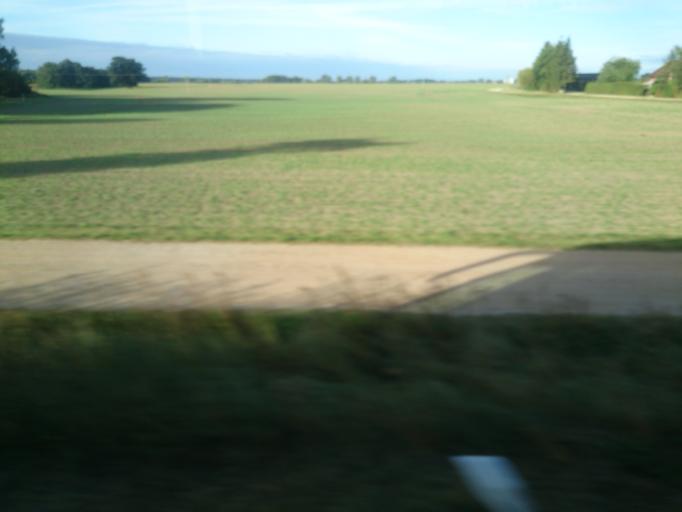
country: DE
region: Mecklenburg-Vorpommern
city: Zussow
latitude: 53.9832
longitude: 13.6075
